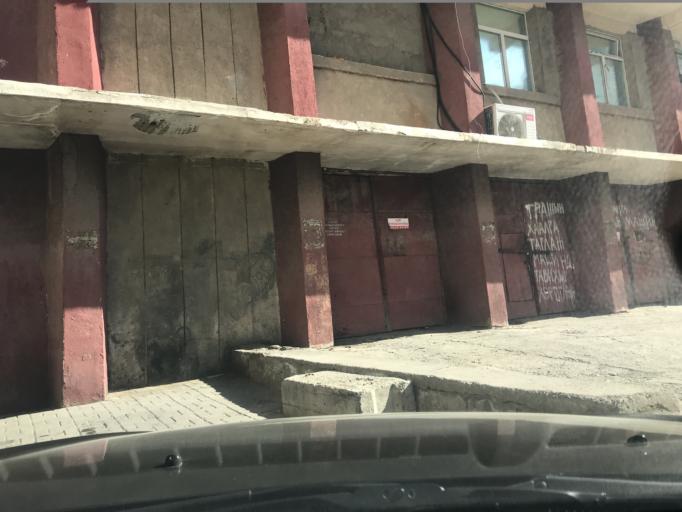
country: MN
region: Ulaanbaatar
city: Ulaanbaatar
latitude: 47.9167
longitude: 106.9019
